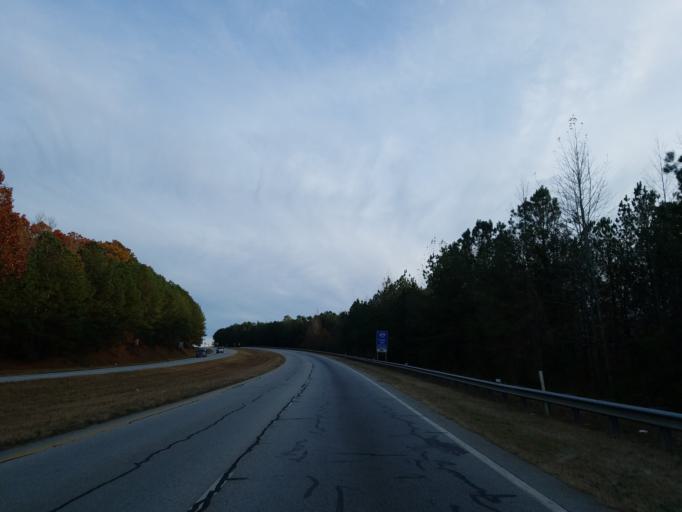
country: US
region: Georgia
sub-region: Haralson County
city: Bremen
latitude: 33.6986
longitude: -85.1574
